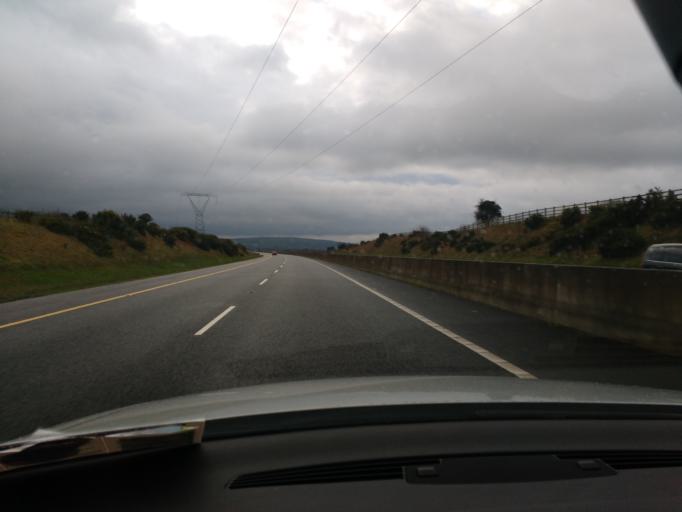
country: IE
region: Munster
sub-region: North Tipperary
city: Nenagh
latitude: 52.8250
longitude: -8.3011
